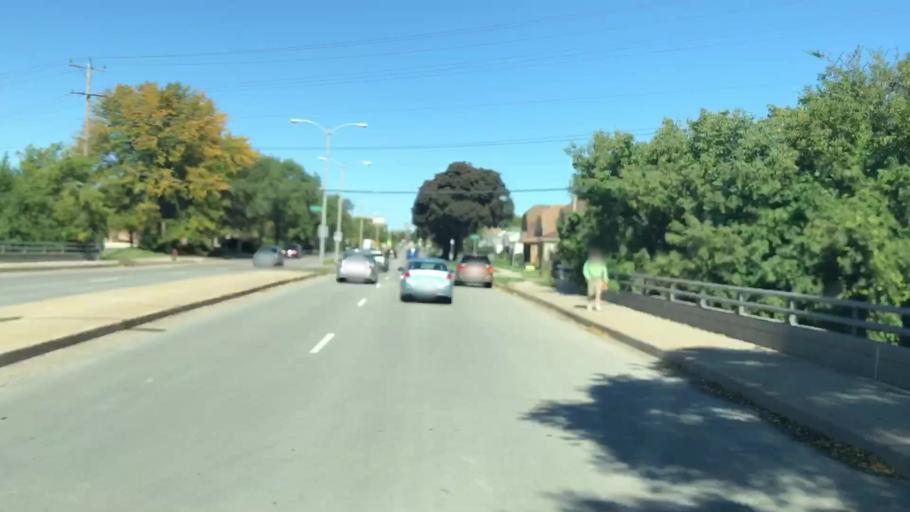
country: US
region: Wisconsin
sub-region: Milwaukee County
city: Saint Francis
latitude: 42.9841
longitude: -87.9094
